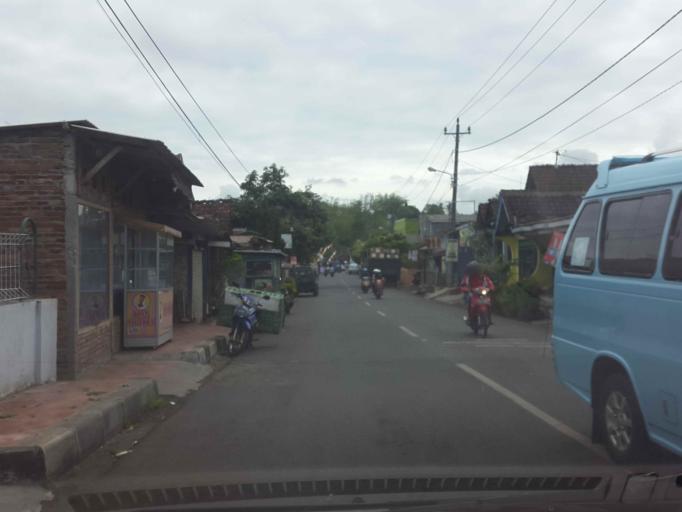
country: ID
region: Central Java
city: Salatiga
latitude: -7.3334
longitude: 110.5119
